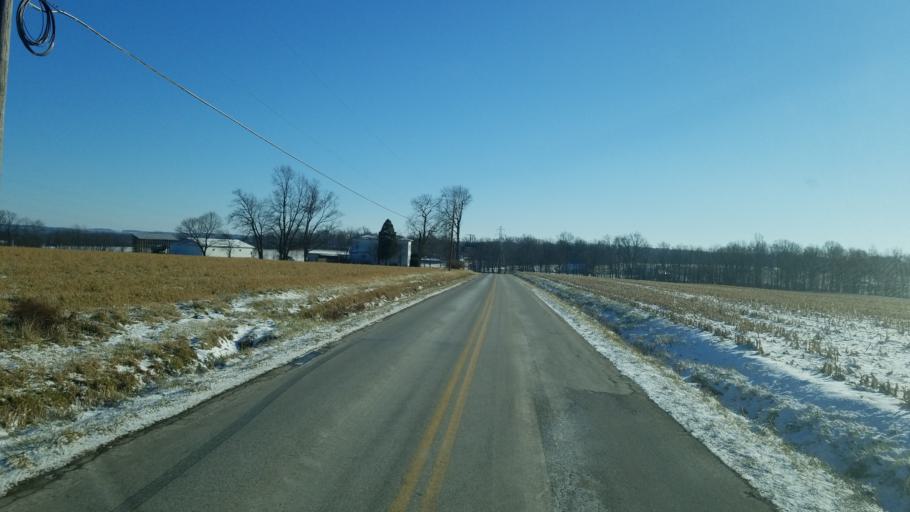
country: US
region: Ohio
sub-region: Wayne County
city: Apple Creek
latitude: 40.7705
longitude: -81.8916
